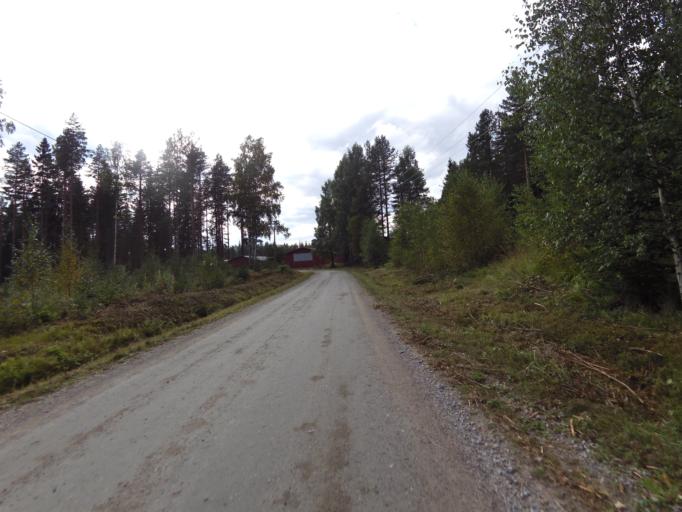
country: SE
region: Gaevleborg
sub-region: Sandvikens Kommun
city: Sandviken
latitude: 60.7156
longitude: 16.8073
